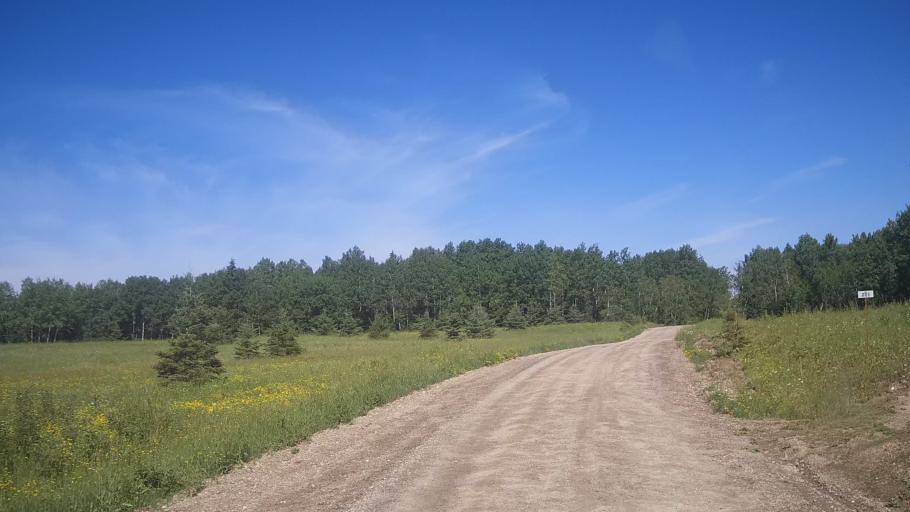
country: CA
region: Ontario
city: Dryden
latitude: 49.8193
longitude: -93.3363
